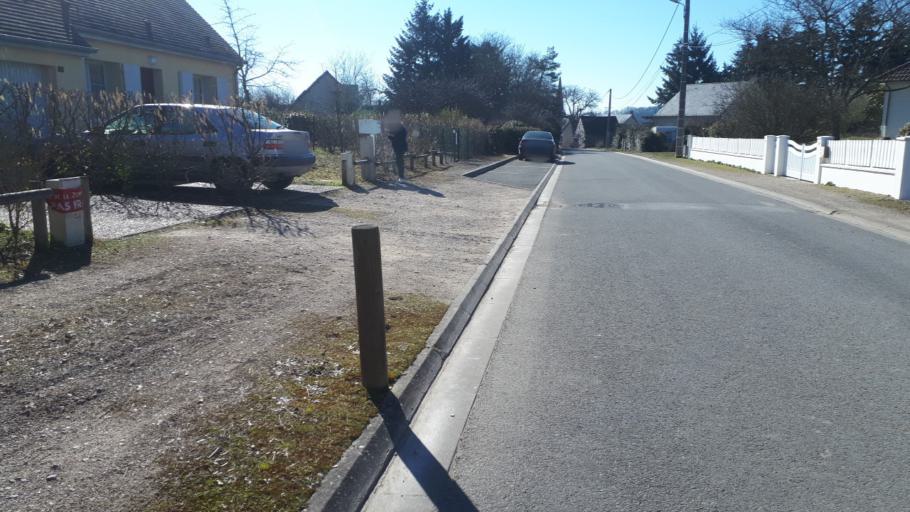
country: FR
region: Centre
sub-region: Departement du Loir-et-Cher
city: Villiers-sur-Loir
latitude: 47.7899
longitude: 0.9682
